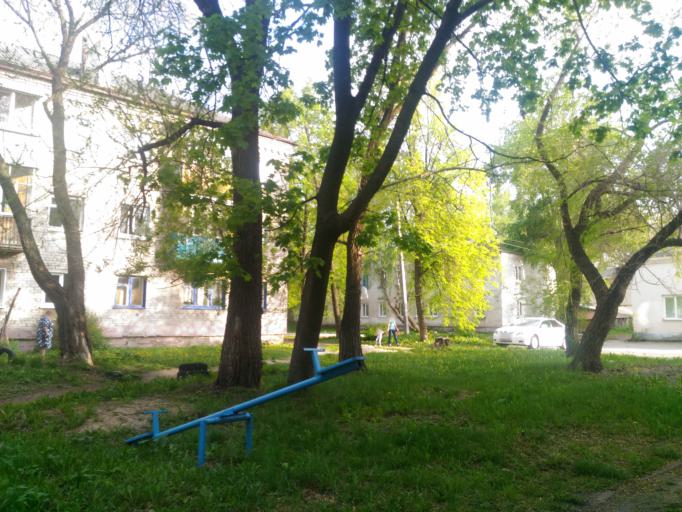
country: RU
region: Ulyanovsk
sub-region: Ulyanovskiy Rayon
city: Ulyanovsk
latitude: 54.2768
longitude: 48.3405
